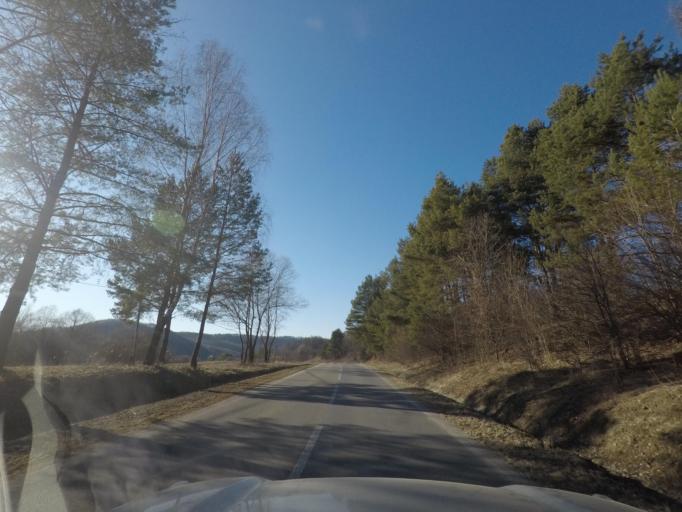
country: SK
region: Presovsky
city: Medzilaborce
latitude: 49.2508
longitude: 21.9222
